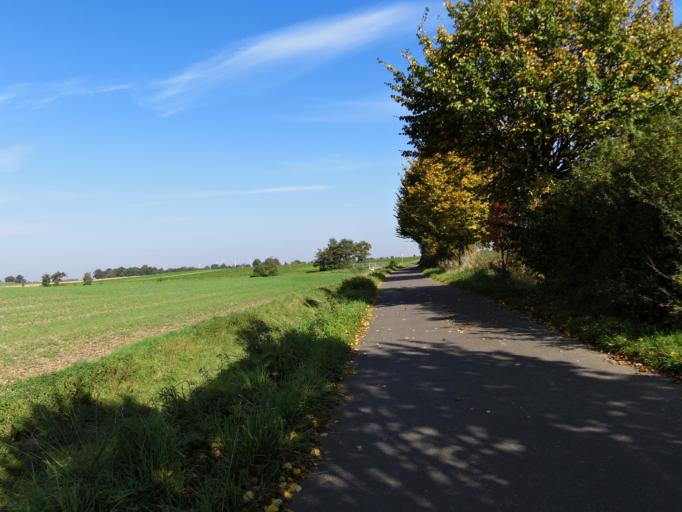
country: DE
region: North Rhine-Westphalia
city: Baesweiler
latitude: 50.9301
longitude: 6.1776
